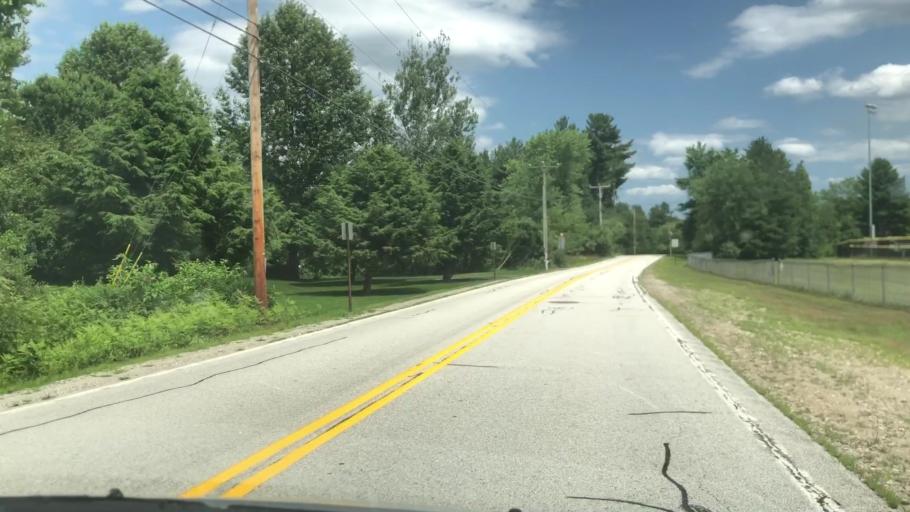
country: US
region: New Hampshire
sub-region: Hillsborough County
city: Bedford
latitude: 42.9383
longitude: -71.4993
